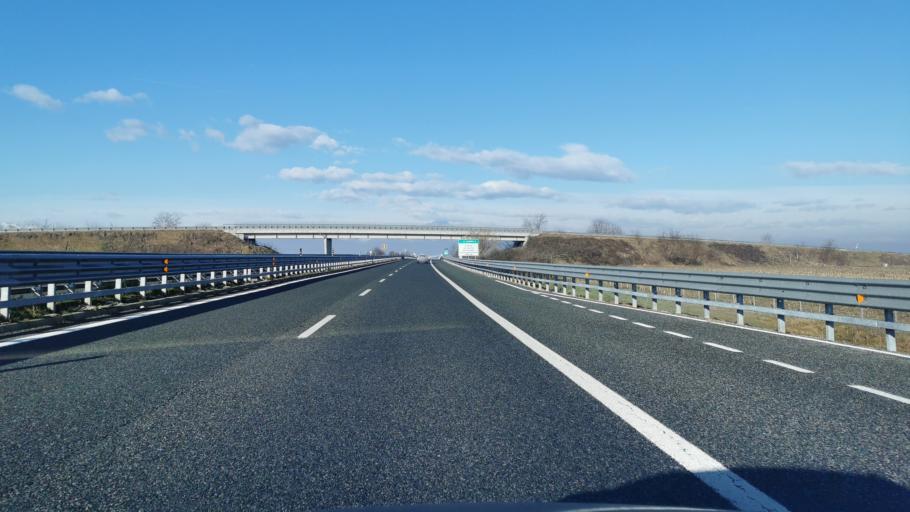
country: IT
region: Piedmont
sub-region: Provincia di Cuneo
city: Sant'Albano Stura
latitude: 44.4707
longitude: 7.7112
